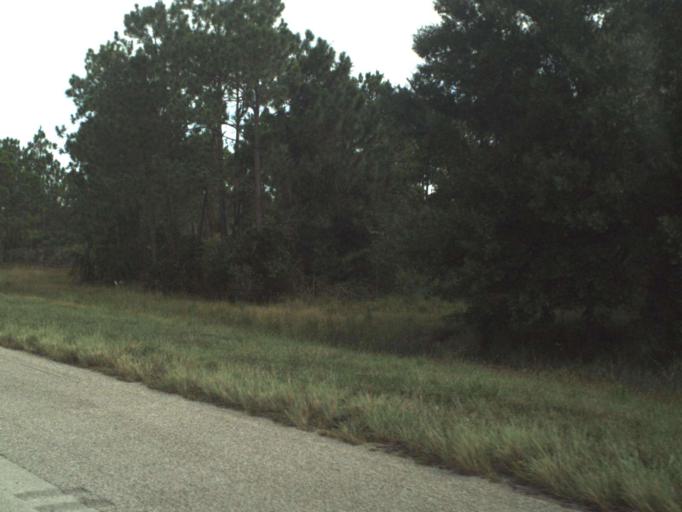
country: US
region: Florida
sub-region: Martin County
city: Palm City
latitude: 27.1351
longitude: -80.3590
